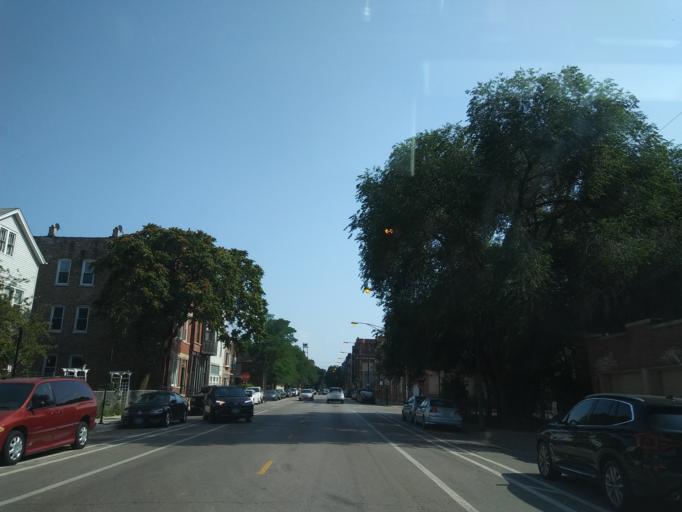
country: US
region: Illinois
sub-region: Cook County
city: Chicago
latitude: 41.8957
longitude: -87.6624
